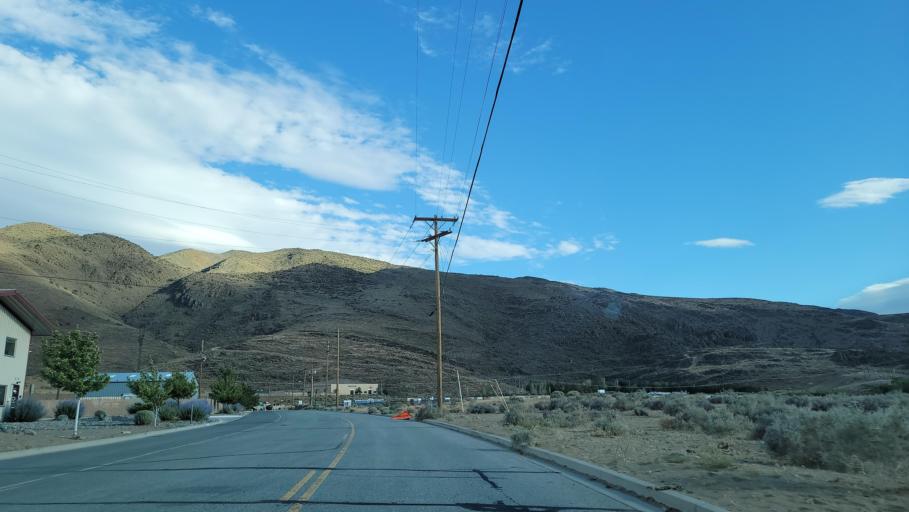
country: US
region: Nevada
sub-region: Washoe County
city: Spanish Springs
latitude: 39.5515
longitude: -119.5542
